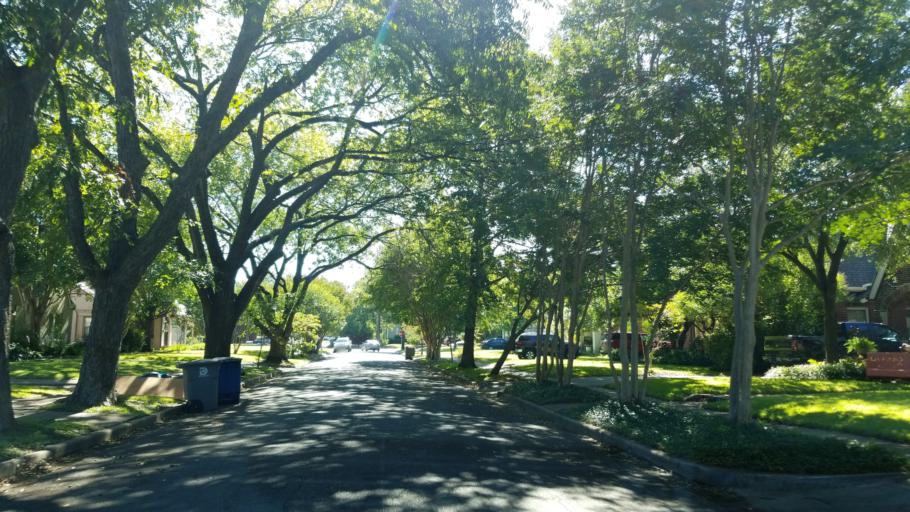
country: US
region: Texas
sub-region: Dallas County
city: Highland Park
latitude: 32.8111
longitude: -96.7548
